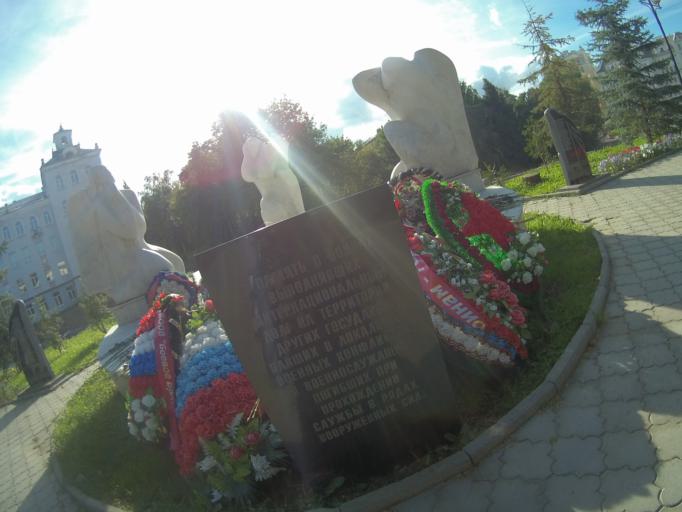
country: RU
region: Vladimir
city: Vladimir
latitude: 56.1311
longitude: 40.3921
